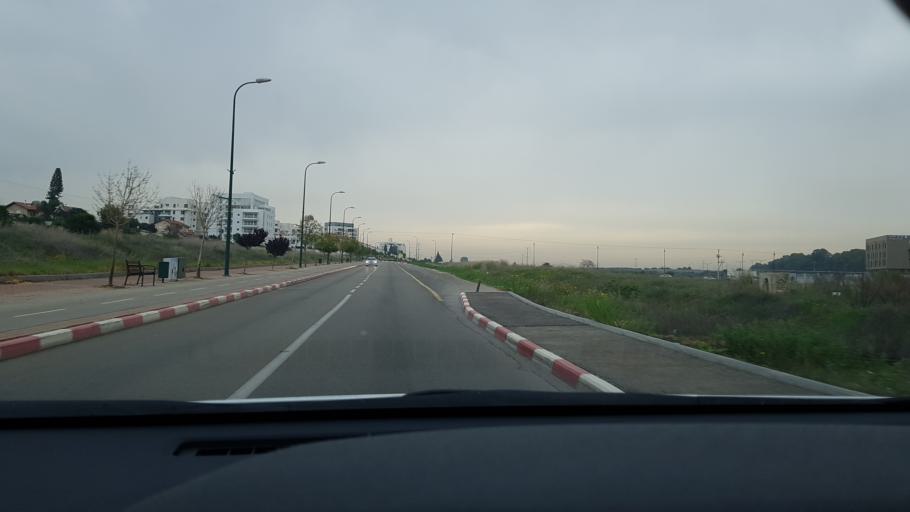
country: IL
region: Central District
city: Ness Ziona
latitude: 31.9209
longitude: 34.8015
